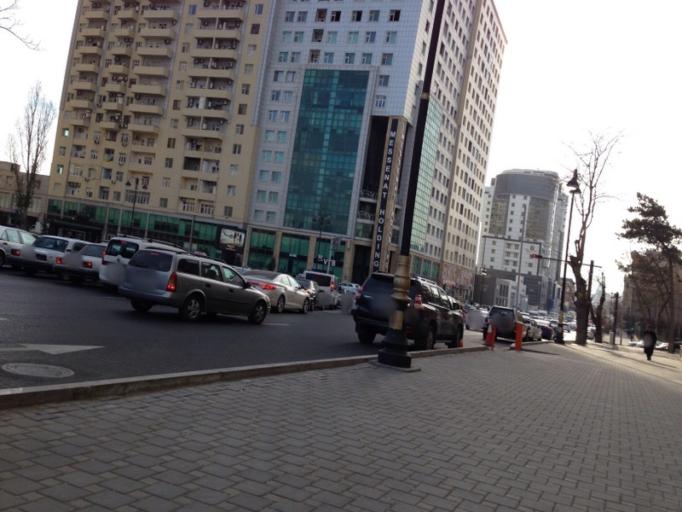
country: AZ
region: Baki
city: Baku
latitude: 40.3923
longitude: 49.8631
